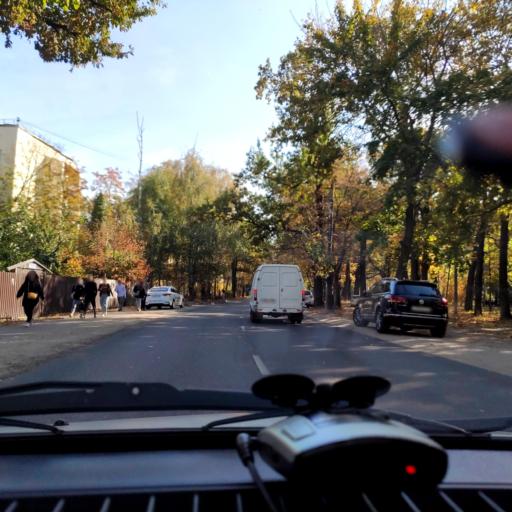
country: RU
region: Voronezj
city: Voronezh
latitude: 51.7215
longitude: 39.2183
